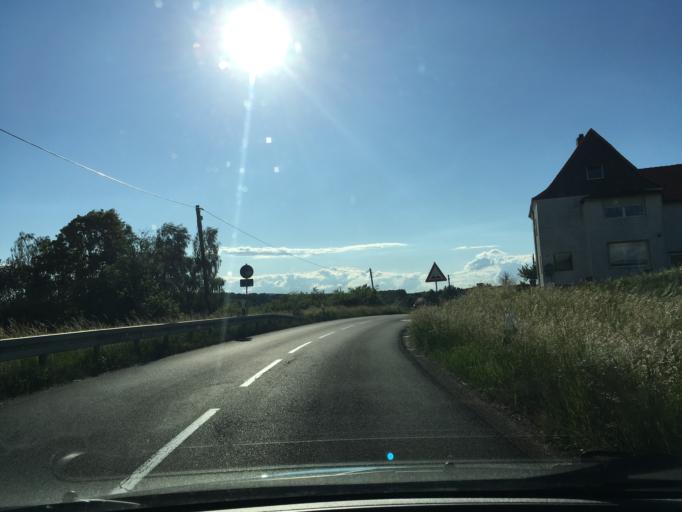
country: DE
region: Lower Saxony
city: Coppengrave
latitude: 51.9857
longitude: 9.7349
